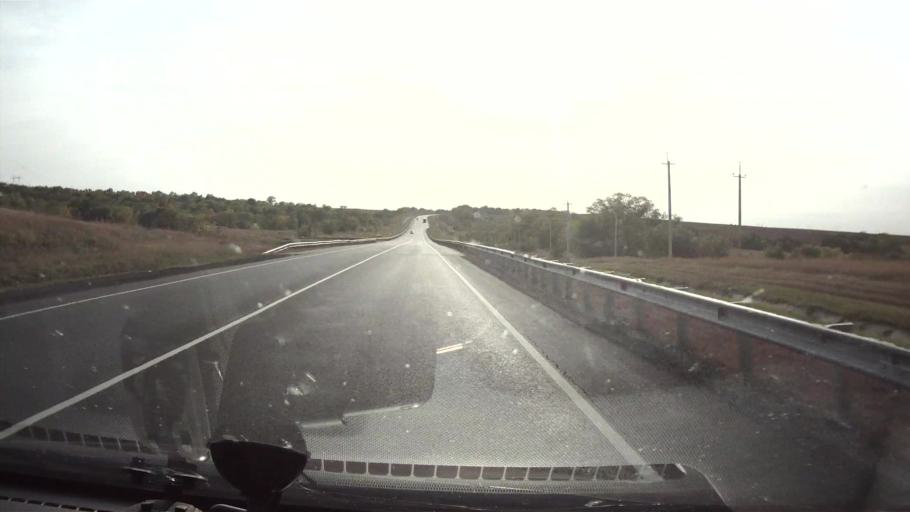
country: RU
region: Saratov
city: Shumeyka
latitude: 51.7849
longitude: 46.1332
